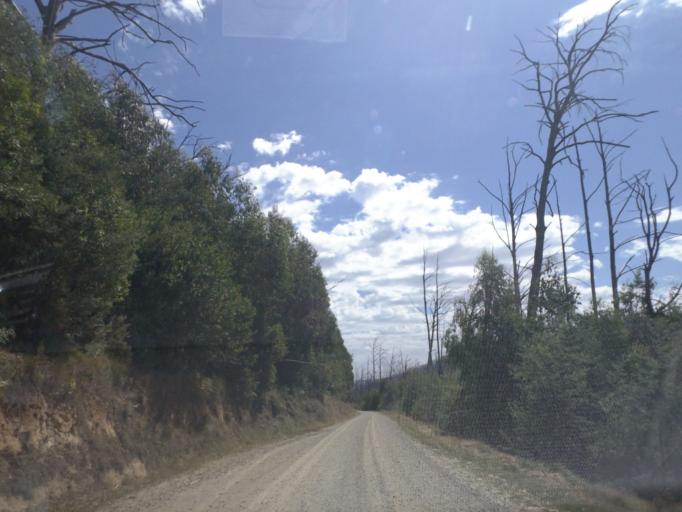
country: AU
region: Victoria
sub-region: Murrindindi
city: Alexandra
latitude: -37.4483
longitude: 145.7924
